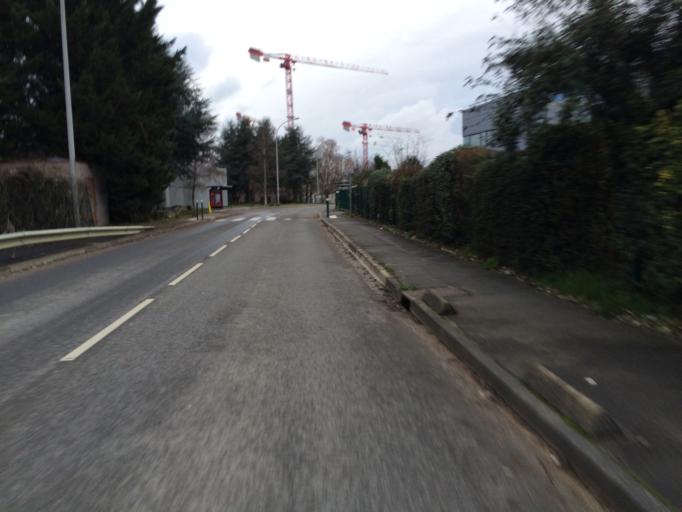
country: FR
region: Ile-de-France
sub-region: Departement de l'Essonne
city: Bures-sur-Yvette
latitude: 48.7093
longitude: 2.1779
